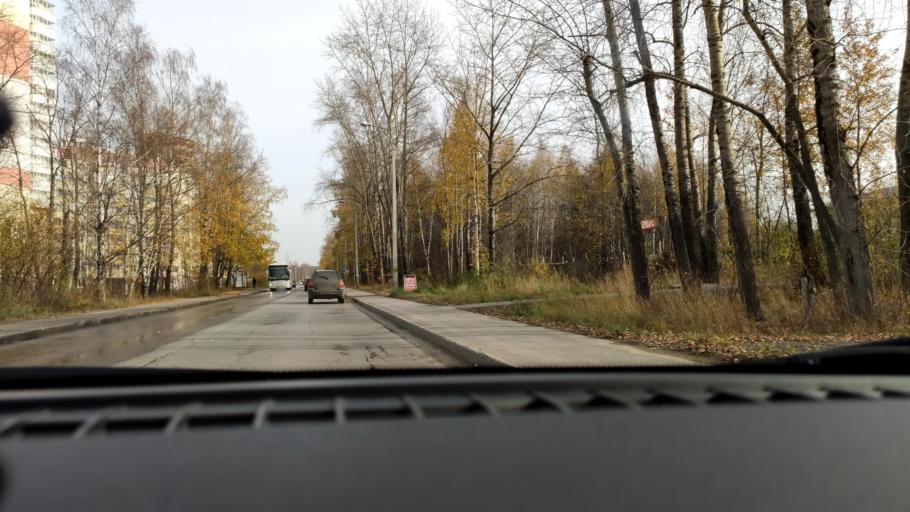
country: RU
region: Perm
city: Polazna
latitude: 58.1315
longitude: 56.3963
